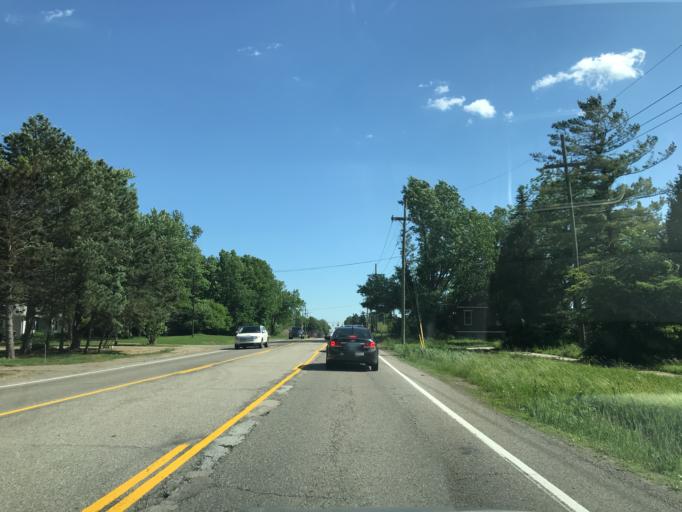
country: US
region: Michigan
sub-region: Oakland County
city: Novi
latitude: 42.4827
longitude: -83.5153
